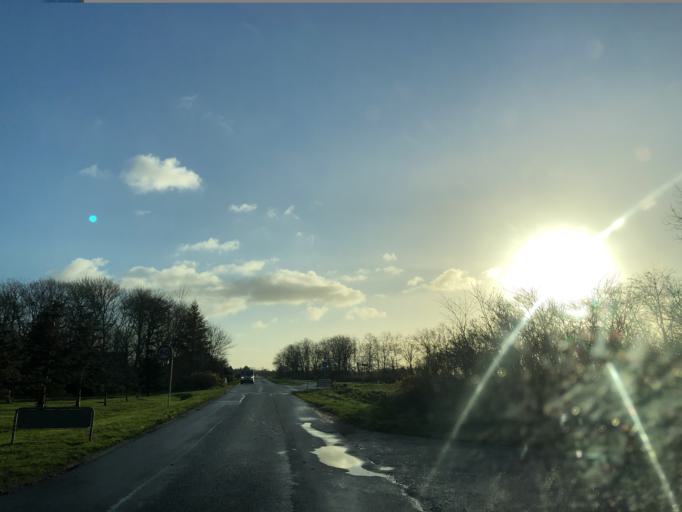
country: DK
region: Central Jutland
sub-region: Holstebro Kommune
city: Ulfborg
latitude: 56.2051
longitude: 8.2579
